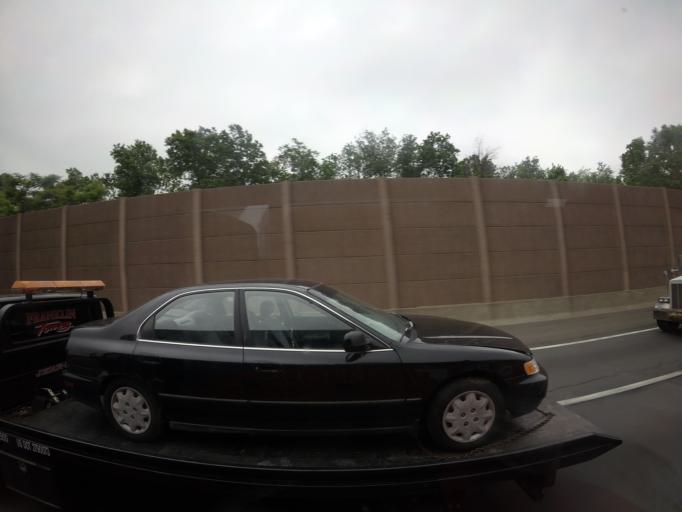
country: US
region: New Jersey
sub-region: Middlesex County
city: Carteret
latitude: 40.5776
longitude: -74.2455
